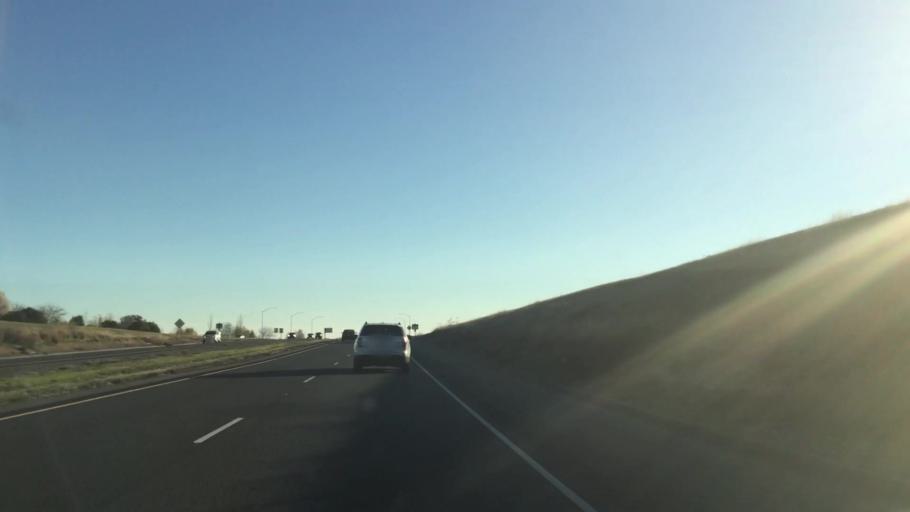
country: US
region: California
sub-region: Yuba County
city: Olivehurst
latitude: 39.0764
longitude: -121.5415
